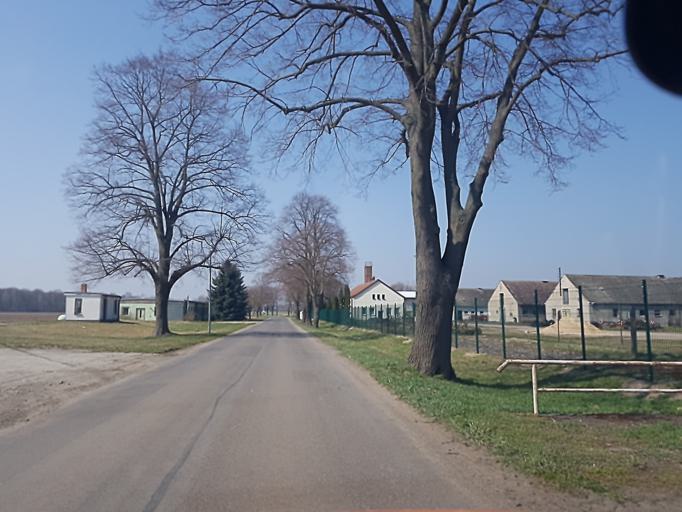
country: DE
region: Brandenburg
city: Forst
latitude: 51.6808
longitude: 14.5524
